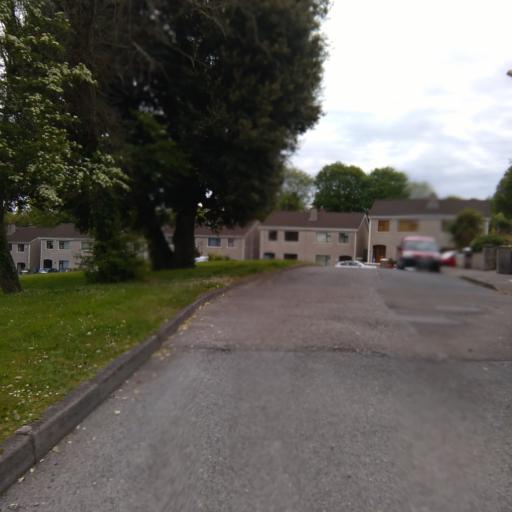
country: IE
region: Munster
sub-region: County Cork
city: Cork
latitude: 51.9130
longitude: -8.4471
